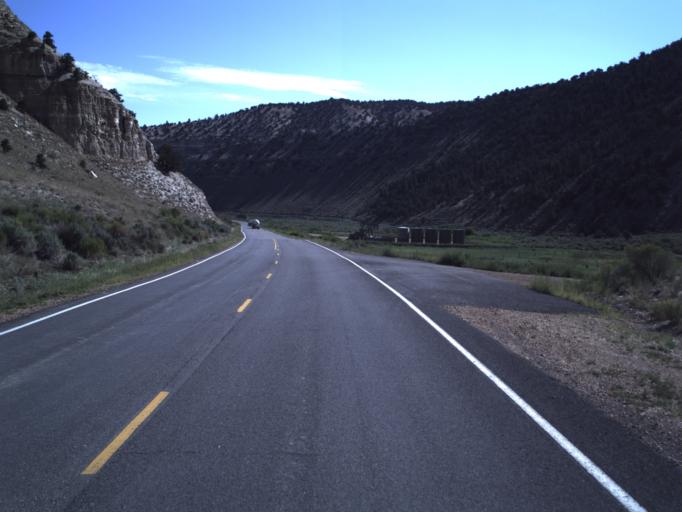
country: US
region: Utah
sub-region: Duchesne County
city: Duchesne
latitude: 40.0312
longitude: -110.5455
